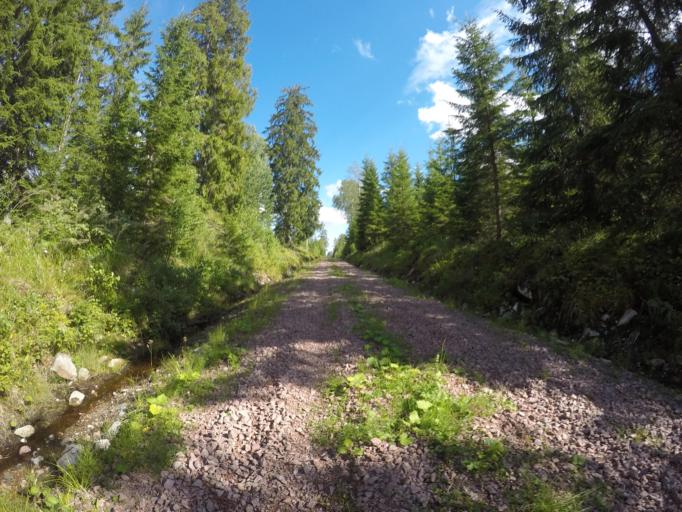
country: SE
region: OErebro
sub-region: Hallefors Kommun
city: Haellefors
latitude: 60.0225
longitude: 14.5771
